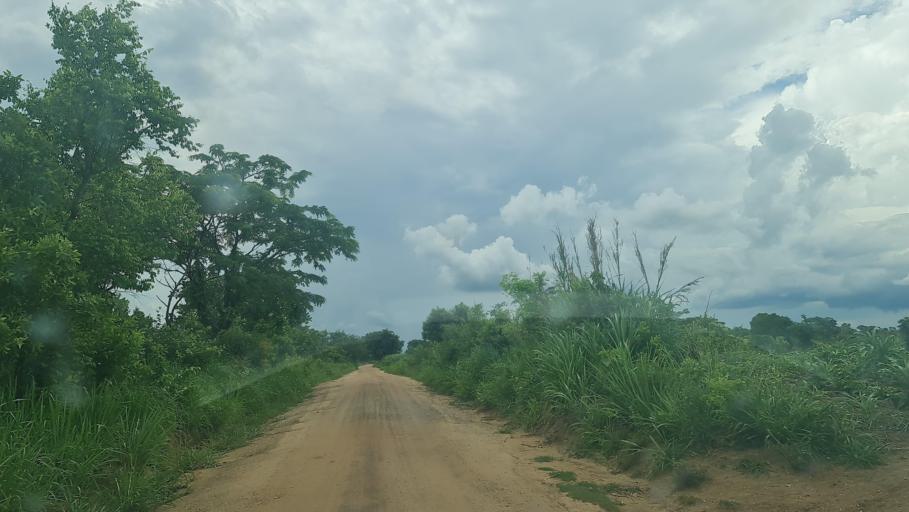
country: MW
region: Southern Region
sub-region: Nsanje District
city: Nsanje
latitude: -17.5876
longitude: 35.6704
